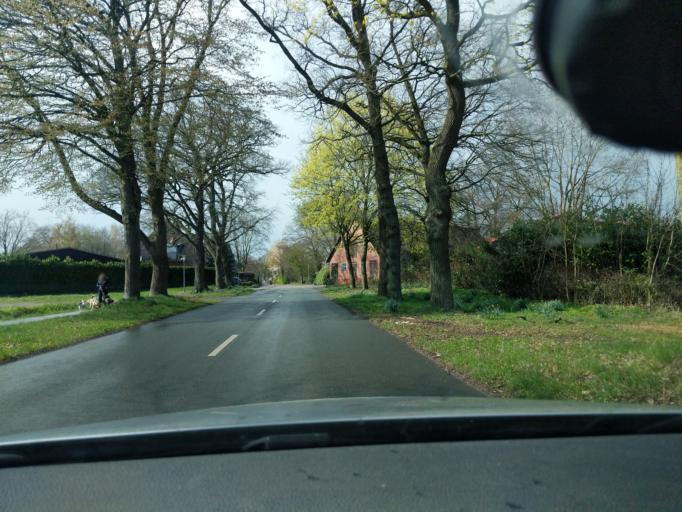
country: DE
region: Lower Saxony
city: Bargstedt
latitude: 53.4583
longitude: 9.4518
